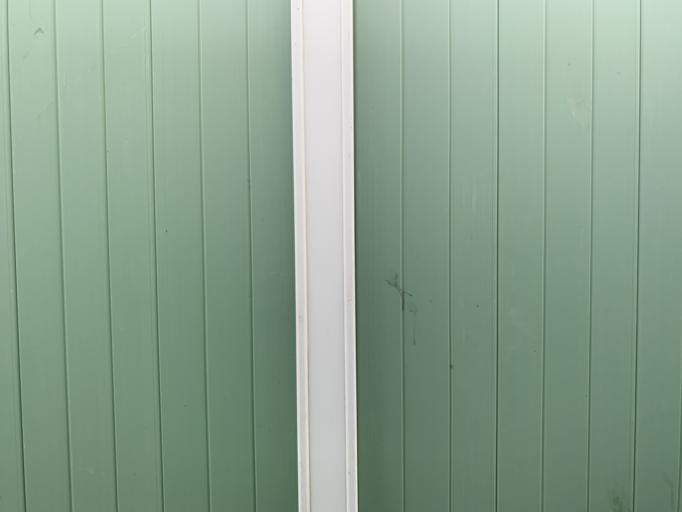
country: CN
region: Shanghai Shi
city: Huamu
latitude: 31.2421
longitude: 121.5749
